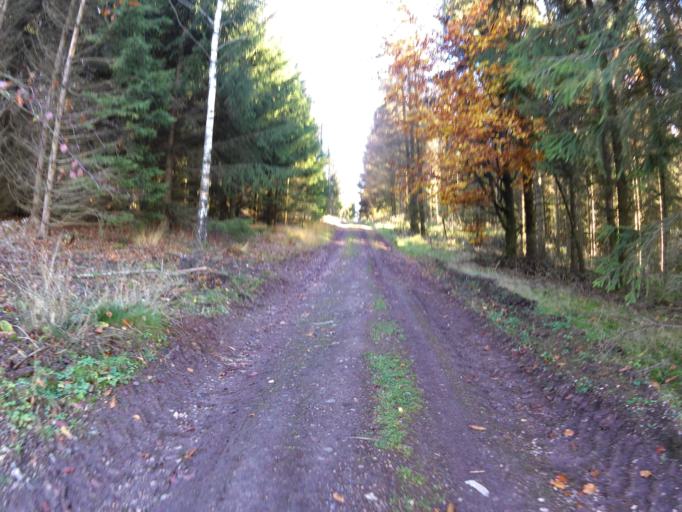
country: DE
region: Thuringia
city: Ruhla
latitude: 50.9054
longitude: 10.3530
